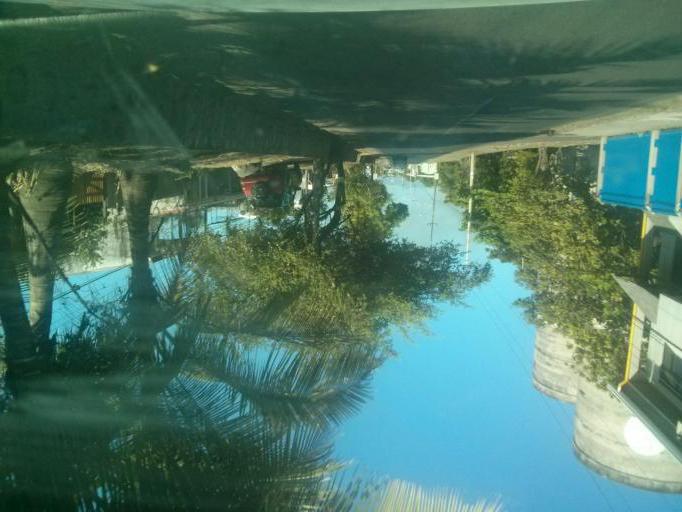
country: CR
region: Puntarenas
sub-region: Canton Central de Puntarenas
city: Puntarenas
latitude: 9.9809
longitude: -84.8105
